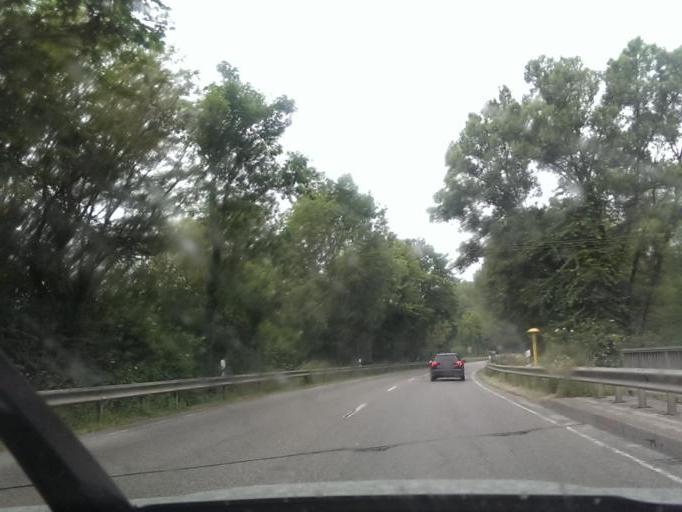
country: DE
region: Bavaria
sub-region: Regierungsbezirk Mittelfranken
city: Greding
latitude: 48.9996
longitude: 11.3868
